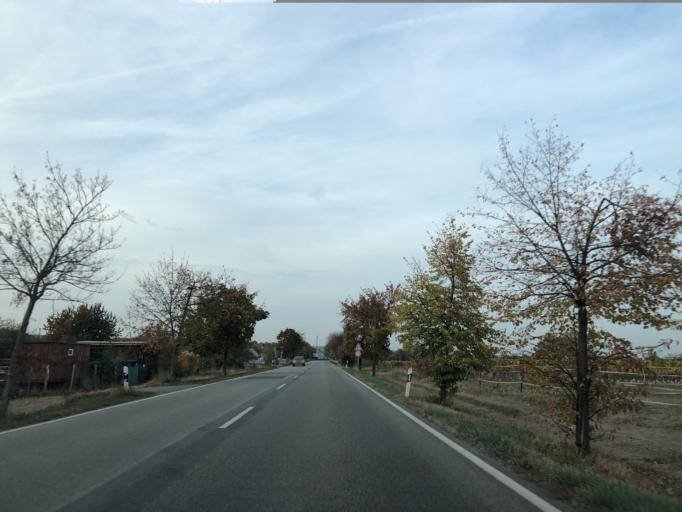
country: DE
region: Rheinland-Pfalz
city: Guntersblum
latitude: 49.7864
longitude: 8.3536
